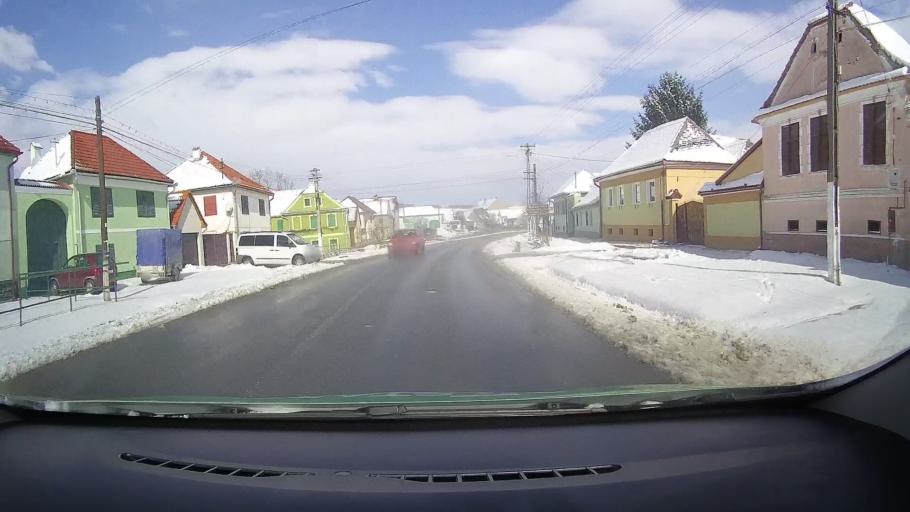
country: RO
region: Sibiu
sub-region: Comuna Altina
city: Altina
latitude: 45.9293
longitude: 24.4629
